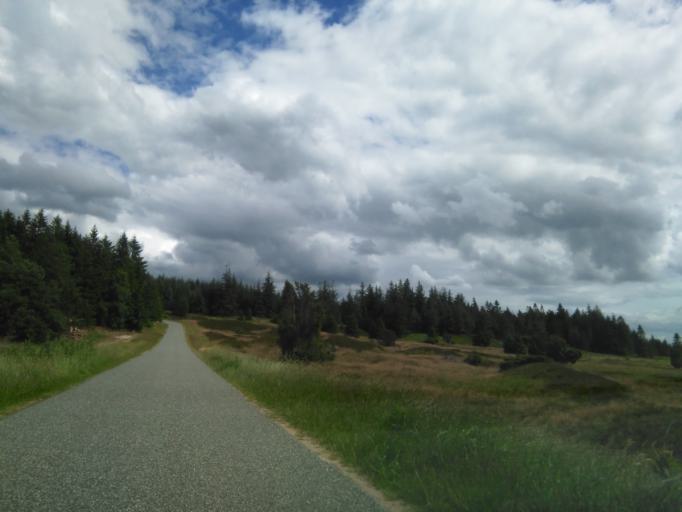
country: DK
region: Central Jutland
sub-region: Silkeborg Kommune
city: Virklund
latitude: 56.0367
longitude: 9.4237
